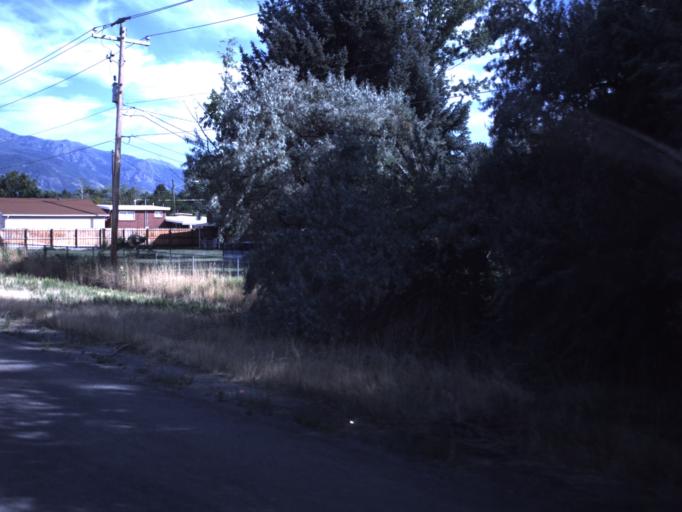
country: US
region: Utah
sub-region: Weber County
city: Washington Terrace
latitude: 41.1676
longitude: -111.9626
